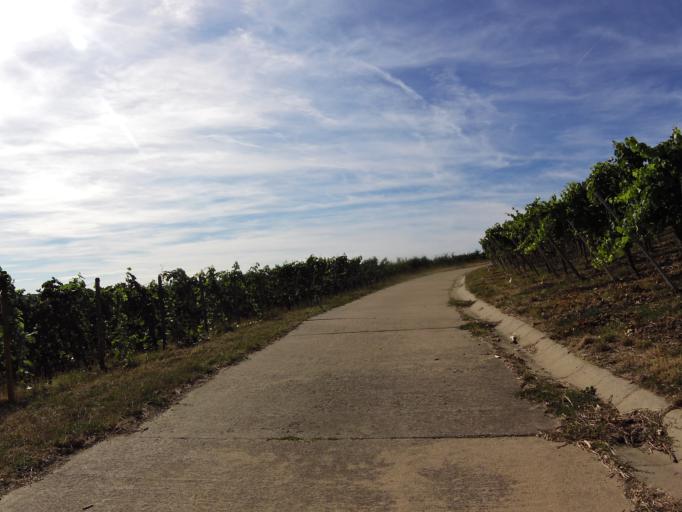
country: DE
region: Bavaria
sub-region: Regierungsbezirk Unterfranken
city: Randersacker
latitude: 49.7451
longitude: 9.9977
